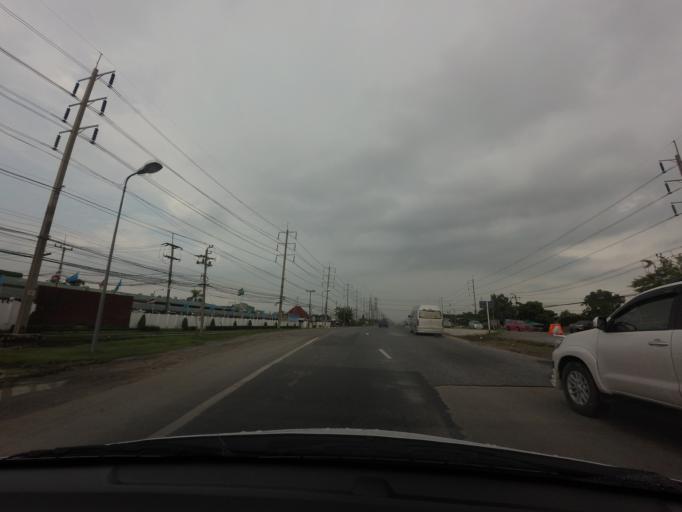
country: TH
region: Bangkok
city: Min Buri
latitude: 13.8107
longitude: 100.7981
